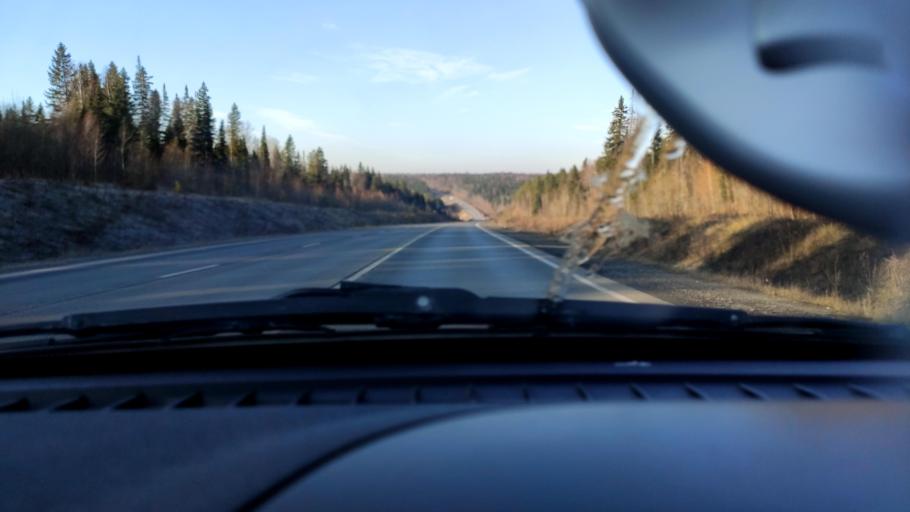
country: RU
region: Perm
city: Novyye Lyady
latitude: 58.0332
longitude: 56.4795
